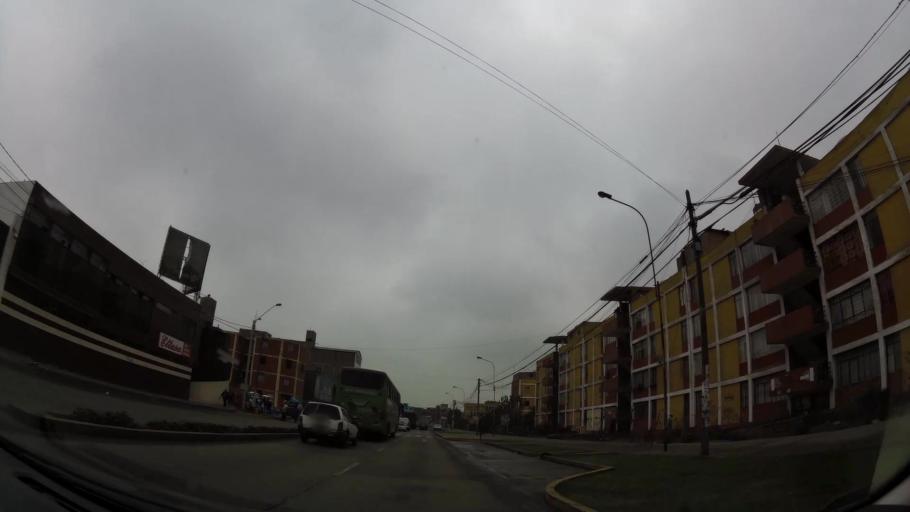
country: PE
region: Lima
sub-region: Lima
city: San Luis
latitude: -12.0722
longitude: -77.0216
